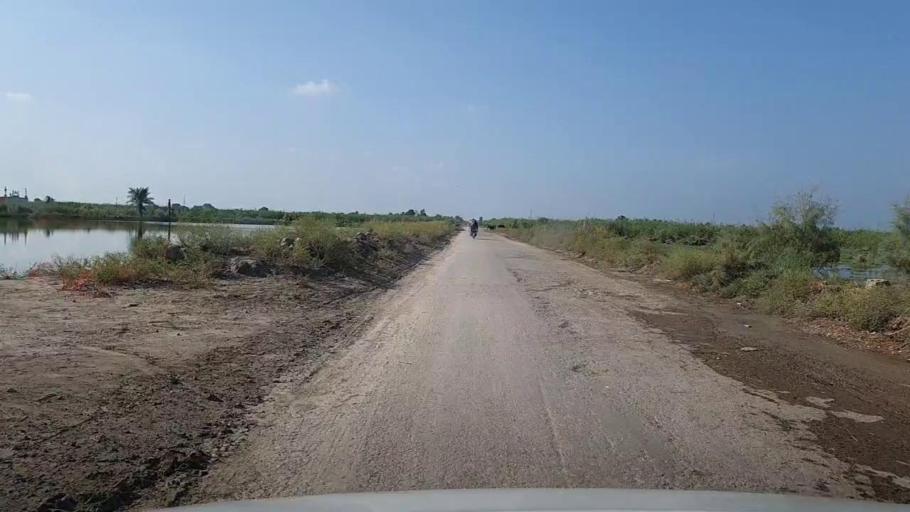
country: PK
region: Sindh
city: Kandiaro
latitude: 27.0656
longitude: 68.3152
